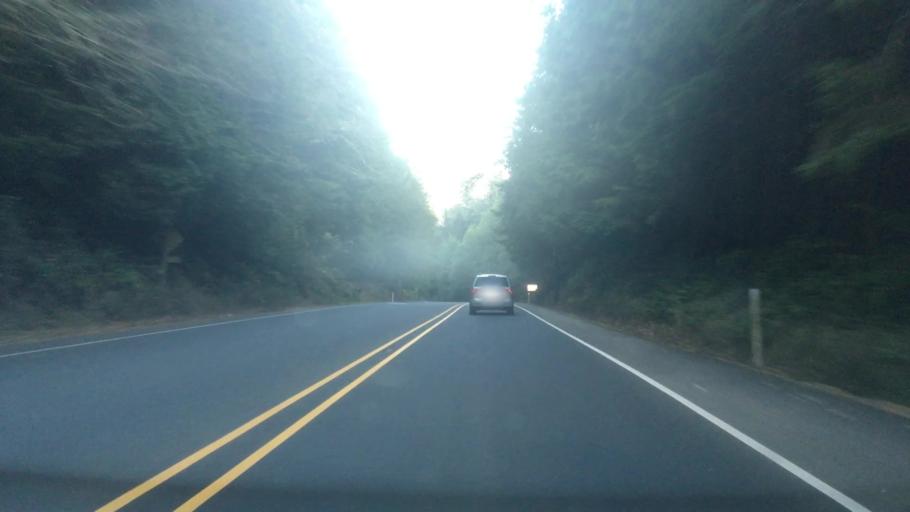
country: US
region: Oregon
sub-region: Clatsop County
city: Cannon Beach
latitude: 45.7804
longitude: -123.9548
